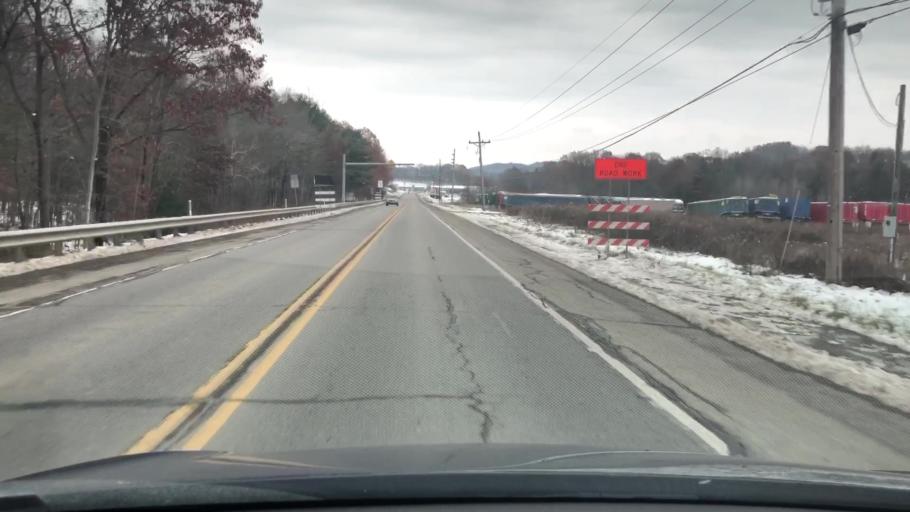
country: US
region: Pennsylvania
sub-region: Jefferson County
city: Brookville
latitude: 41.1618
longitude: -79.0982
